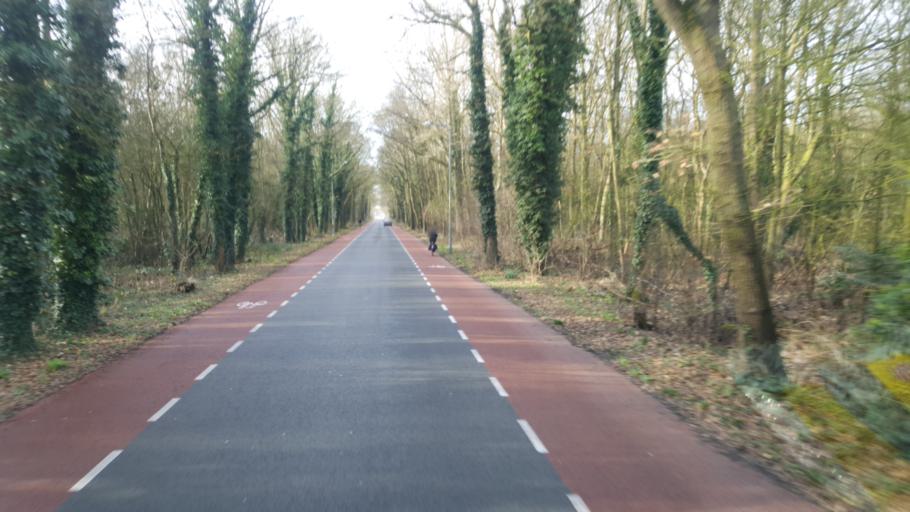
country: NL
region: North Holland
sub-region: Gemeente Heemskerk
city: Heemskerk
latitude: 52.5159
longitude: 4.6638
